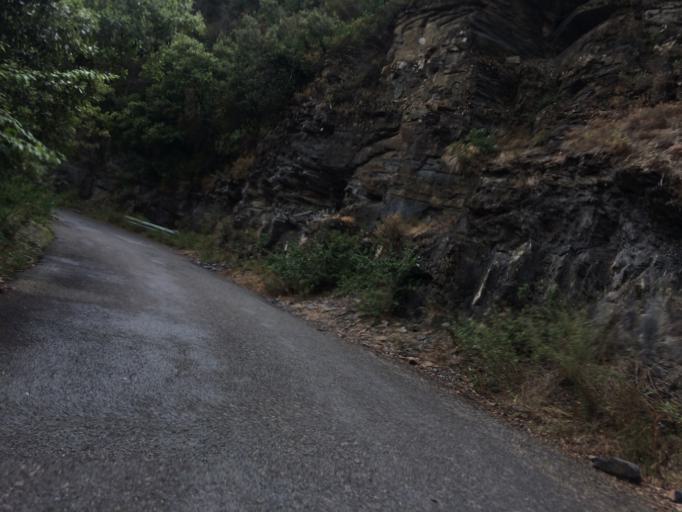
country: IT
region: Liguria
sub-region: Provincia di Imperia
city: Castel Vittorio
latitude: 43.9447
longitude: 7.6962
